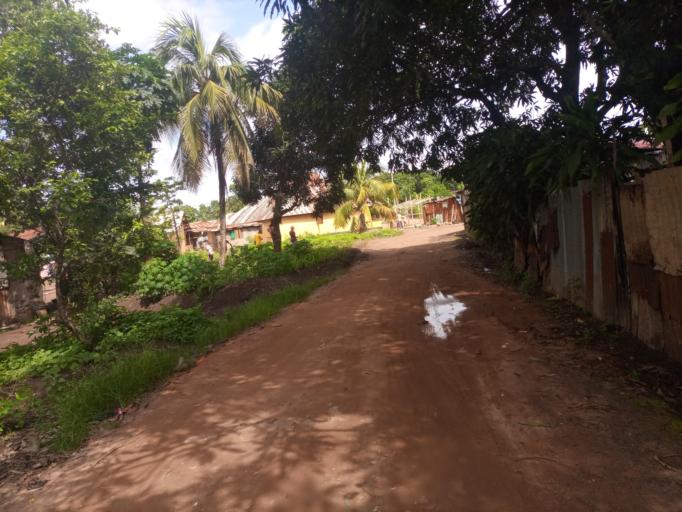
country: SL
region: Northern Province
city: Tintafor
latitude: 8.6282
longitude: -13.2154
